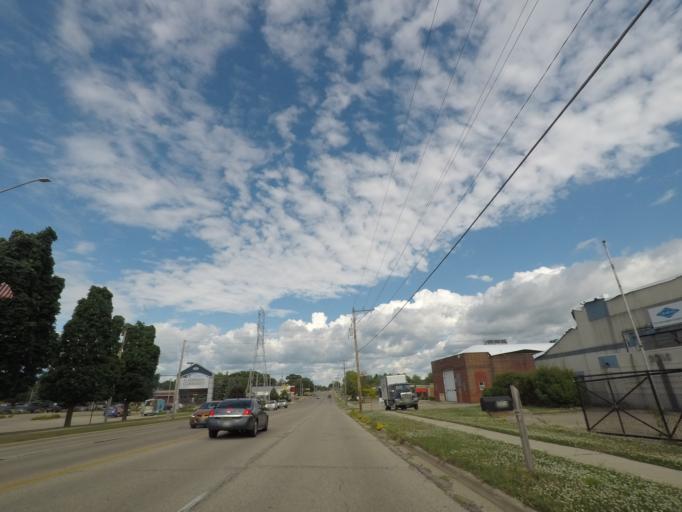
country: US
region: Wisconsin
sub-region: Rock County
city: Janesville
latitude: 42.6792
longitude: -89.0540
